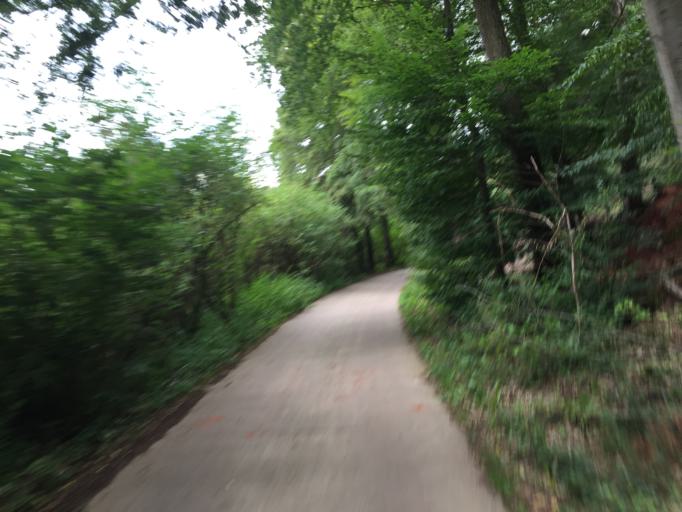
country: DE
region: Hesse
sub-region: Regierungsbezirk Kassel
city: Bad Hersfeld
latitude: 50.8852
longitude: 9.7431
